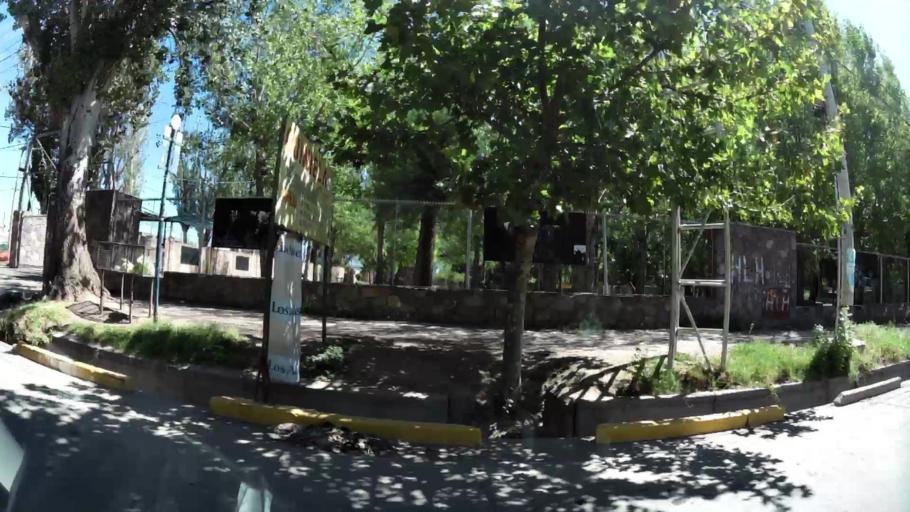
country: AR
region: Mendoza
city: Las Heras
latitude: -32.8460
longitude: -68.8468
